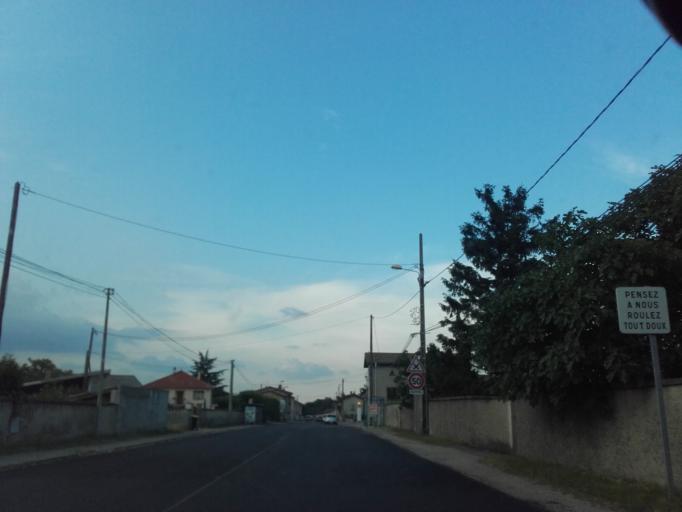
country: FR
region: Rhone-Alpes
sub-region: Departement de l'Isere
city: Auberives-sur-Vareze
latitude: 45.4202
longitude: 4.8168
